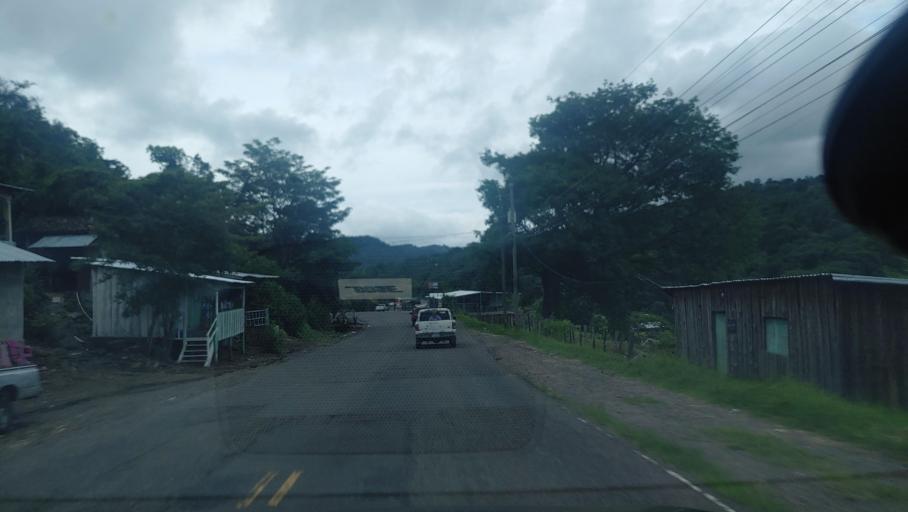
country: HN
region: Choluteca
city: San Marcos de Colon
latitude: 13.3765
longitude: -86.8891
